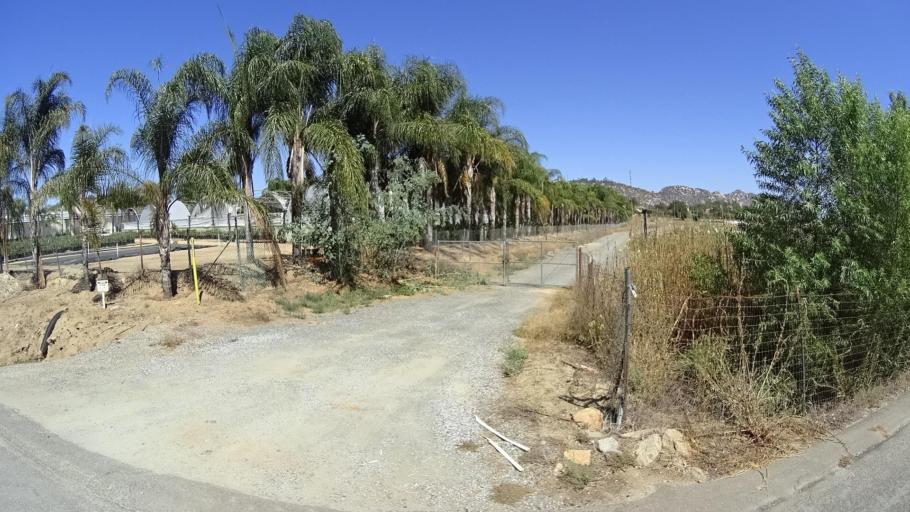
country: US
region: California
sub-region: San Diego County
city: Rainbow
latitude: 33.4081
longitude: -117.1556
